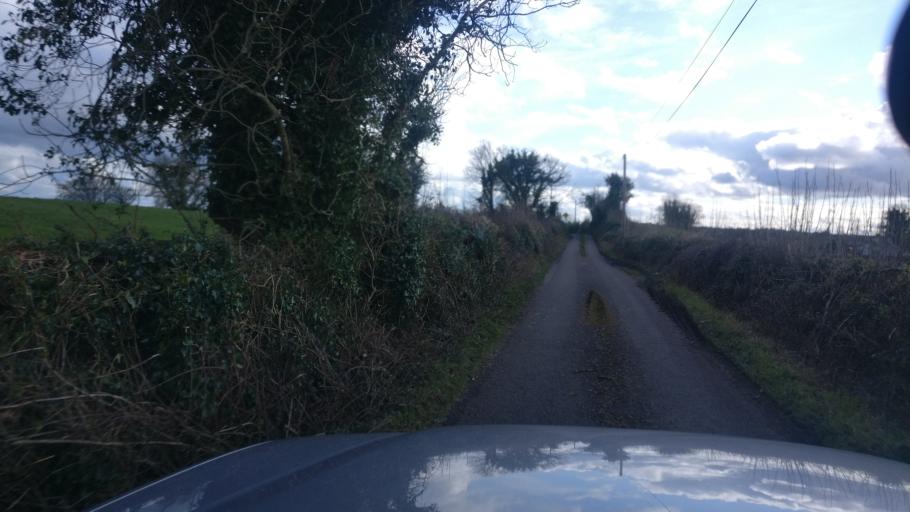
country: IE
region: Connaught
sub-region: County Galway
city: Loughrea
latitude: 53.2014
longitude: -8.4310
